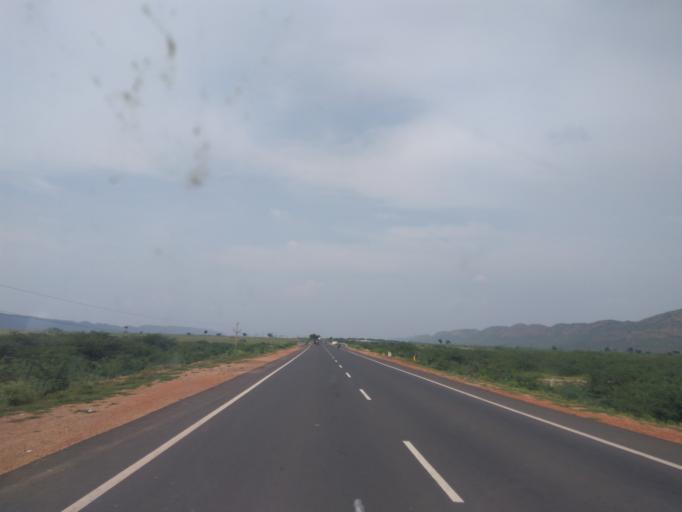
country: IN
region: Andhra Pradesh
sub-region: Prakasam
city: Markapur
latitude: 15.8006
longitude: 79.2594
